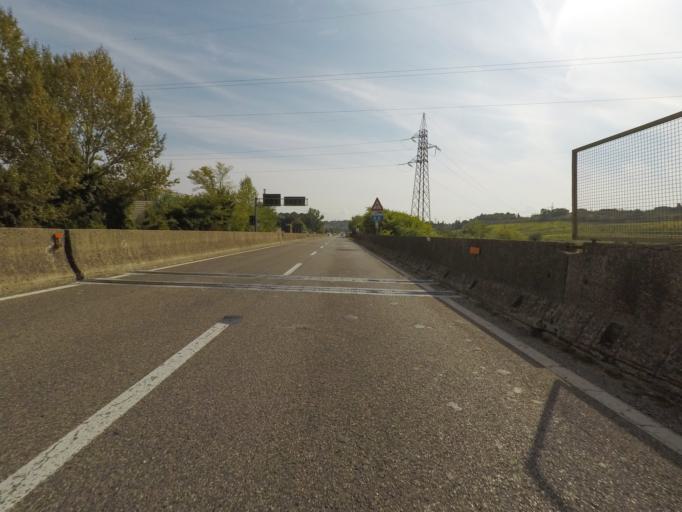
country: IT
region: Tuscany
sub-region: Provincia di Siena
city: Siena
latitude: 43.2989
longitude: 11.3278
